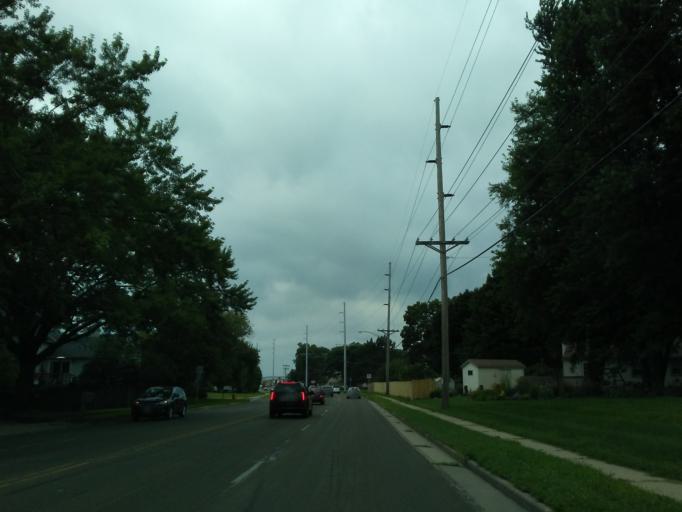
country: US
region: Wisconsin
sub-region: Dane County
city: Middleton
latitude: 43.1110
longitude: -89.5057
